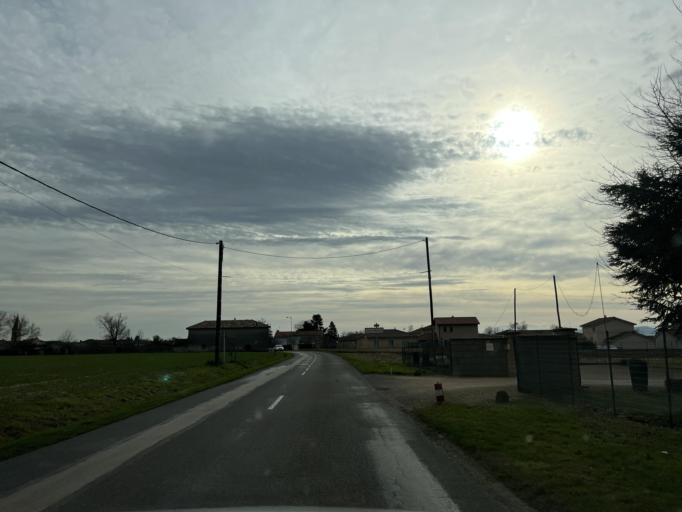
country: FR
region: Rhone-Alpes
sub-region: Departement de l'Ain
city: Villeneuve
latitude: 46.0048
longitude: 4.8448
